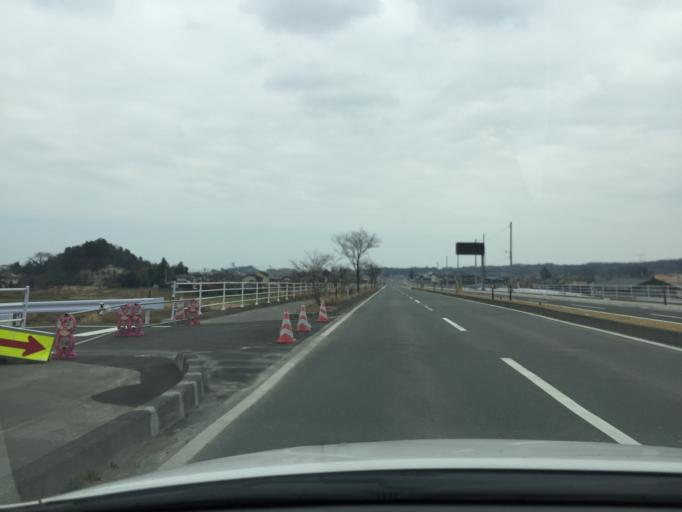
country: JP
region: Miyagi
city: Marumori
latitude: 37.7857
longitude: 140.9065
